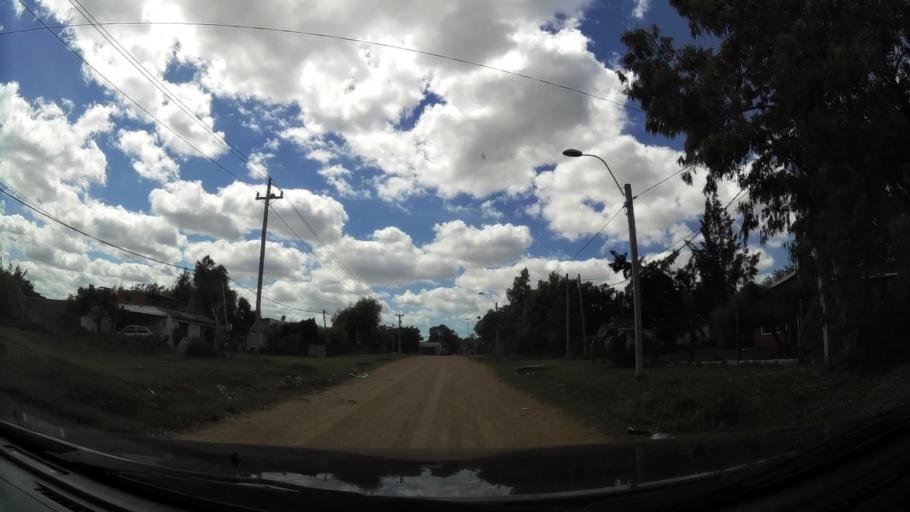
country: UY
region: Canelones
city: Colonia Nicolich
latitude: -34.8156
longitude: -56.0435
